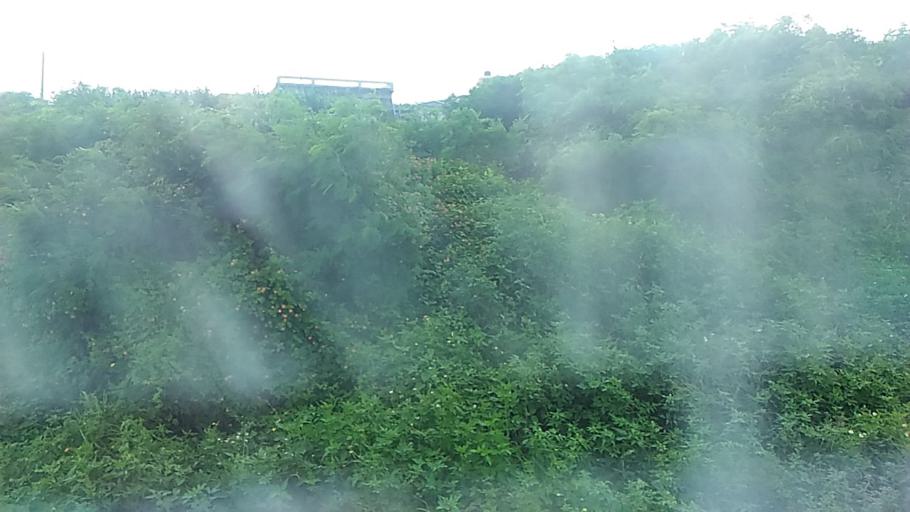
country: TW
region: Taiwan
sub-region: Penghu
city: Ma-kung
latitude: 23.2025
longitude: 119.4339
